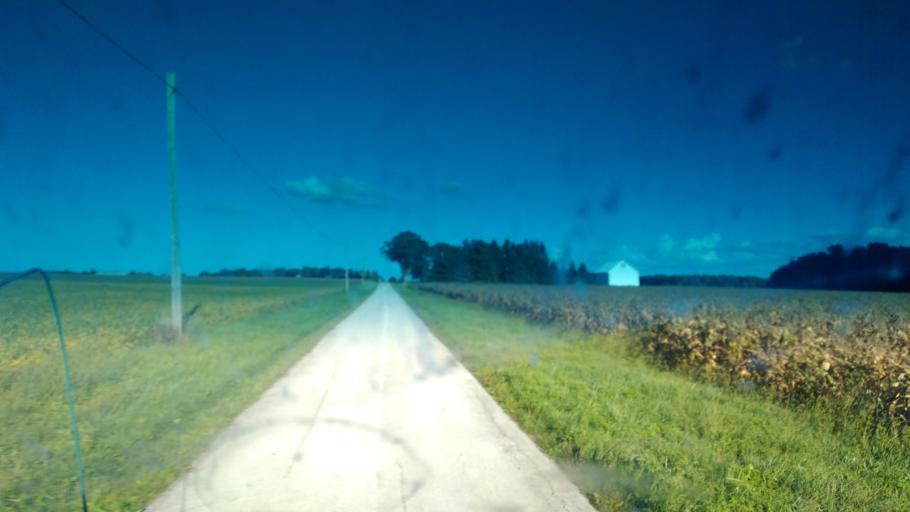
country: US
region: Ohio
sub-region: Wyandot County
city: Carey
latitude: 40.9411
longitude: -83.4760
